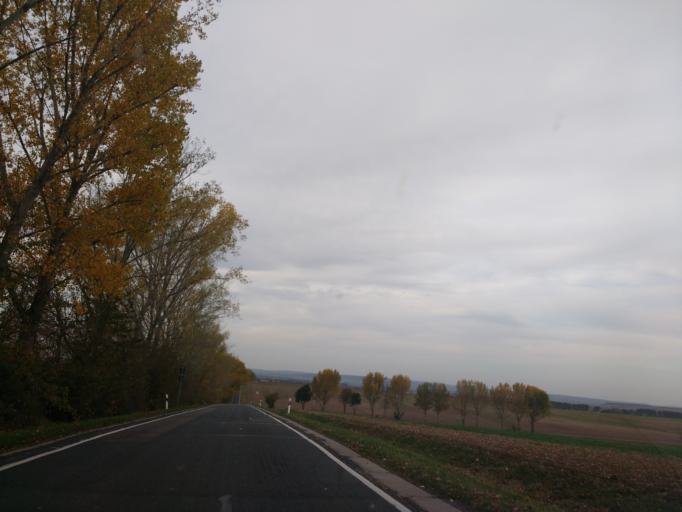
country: DE
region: Thuringia
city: Heroldishausen
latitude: 51.1462
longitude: 10.5220
